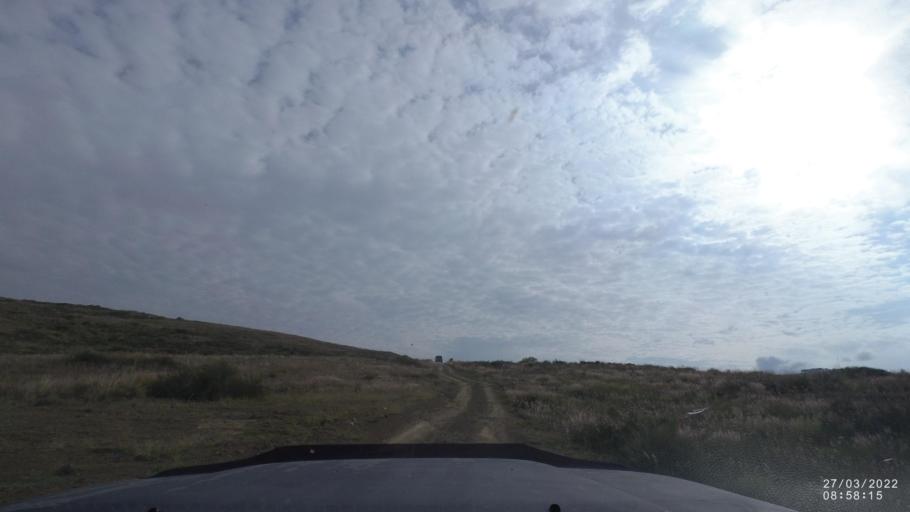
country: BO
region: Cochabamba
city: Cliza
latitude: -17.7435
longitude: -65.8573
